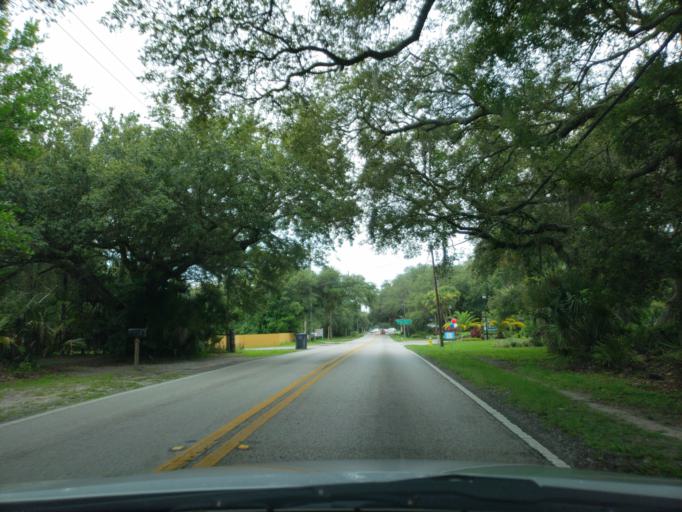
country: US
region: Florida
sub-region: Hillsborough County
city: University
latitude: 28.0939
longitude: -82.4308
